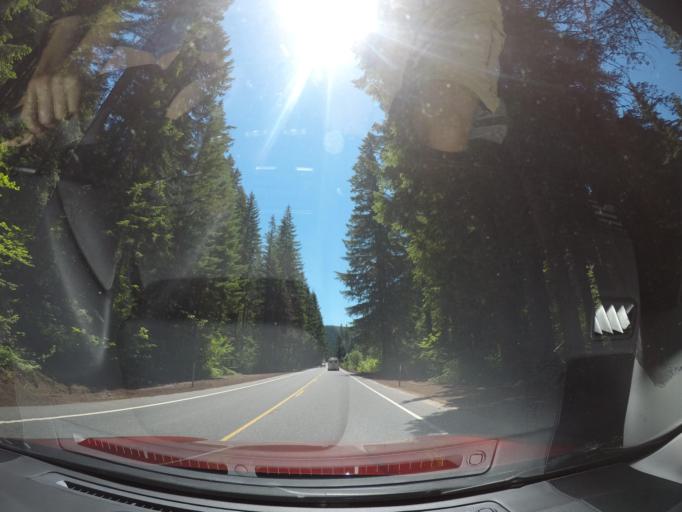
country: US
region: Oregon
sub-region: Linn County
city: Mill City
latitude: 44.5611
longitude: -121.9993
